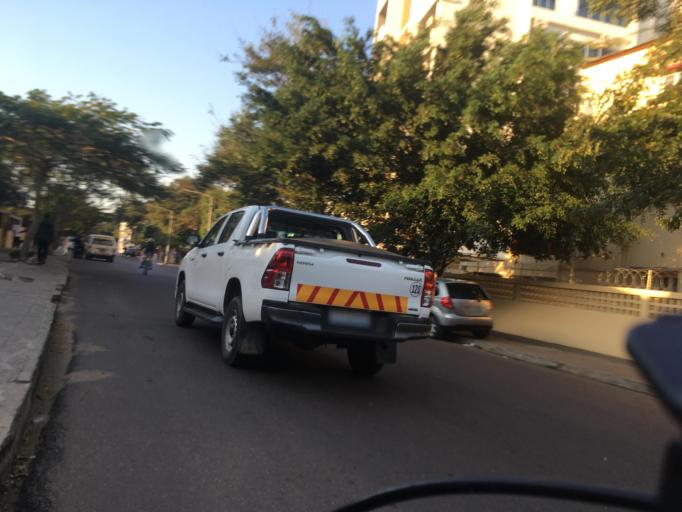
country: MZ
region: Maputo City
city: Maputo
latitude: -25.9730
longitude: 32.5891
